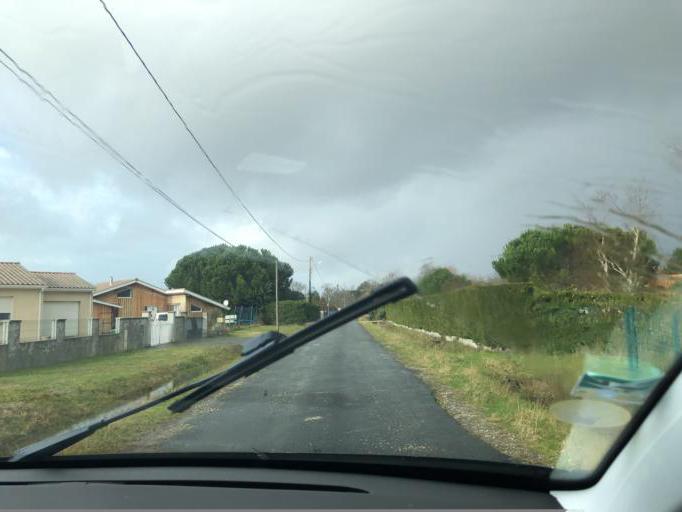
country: FR
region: Aquitaine
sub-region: Departement de la Gironde
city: Hourtin
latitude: 45.1786
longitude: -1.0519
